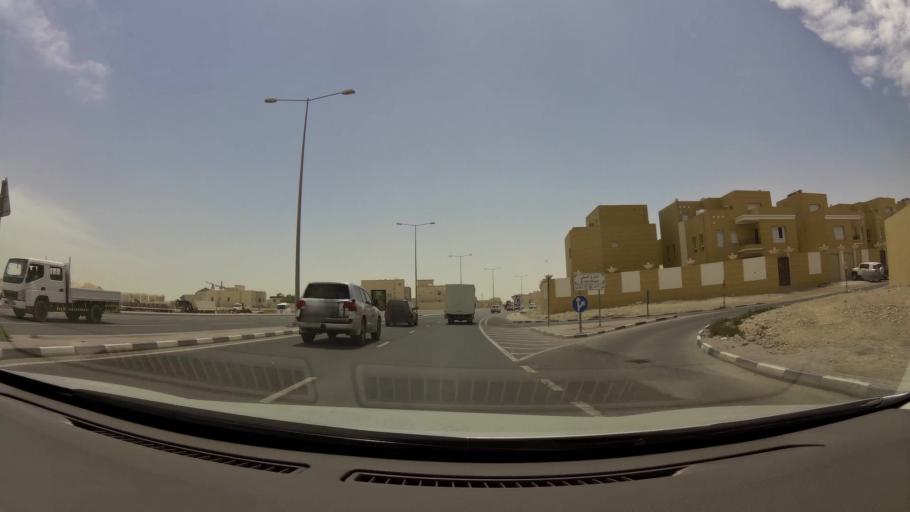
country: QA
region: Baladiyat ar Rayyan
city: Ar Rayyan
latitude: 25.2636
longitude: 51.4205
